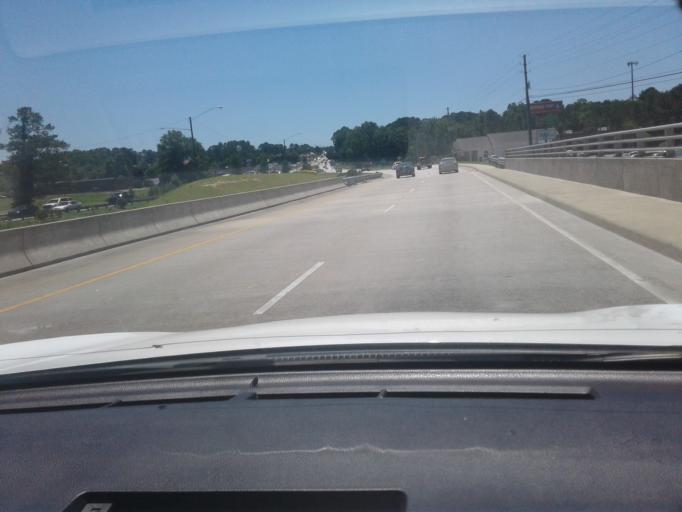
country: US
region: North Carolina
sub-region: Harnett County
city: Lillington
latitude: 35.4067
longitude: -78.8137
